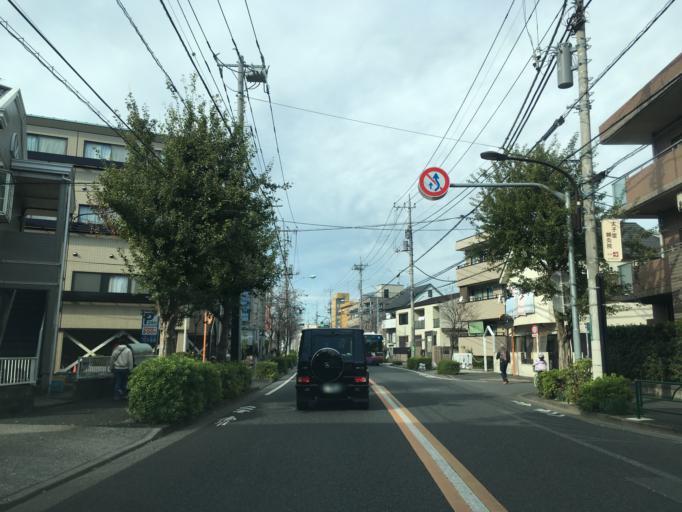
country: JP
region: Tokyo
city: Chofugaoka
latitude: 35.6386
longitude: 139.5735
